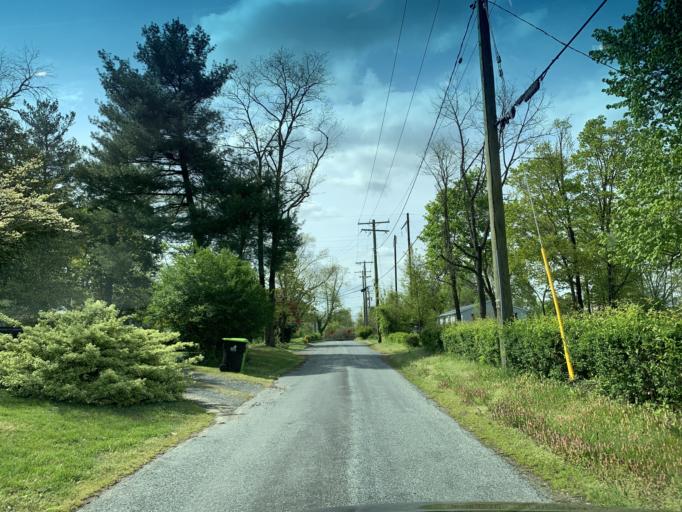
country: US
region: Maryland
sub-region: Harford County
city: Perryman
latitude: 39.4648
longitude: -76.1996
